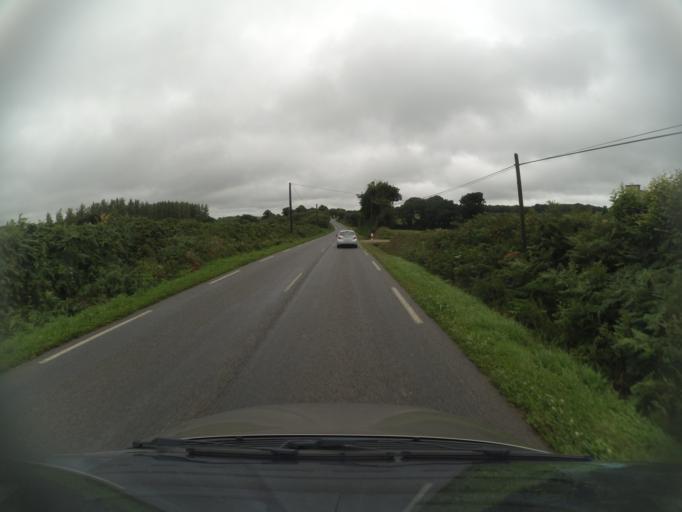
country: FR
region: Brittany
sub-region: Departement du Finistere
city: Lanmeur
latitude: 48.6340
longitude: -3.7320
